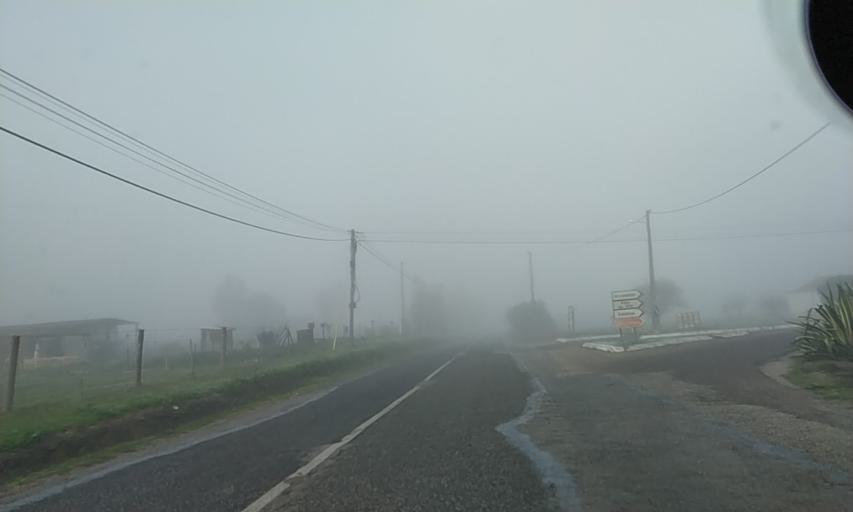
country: PT
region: Setubal
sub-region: Palmela
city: Palmela
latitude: 38.6075
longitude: -8.8556
